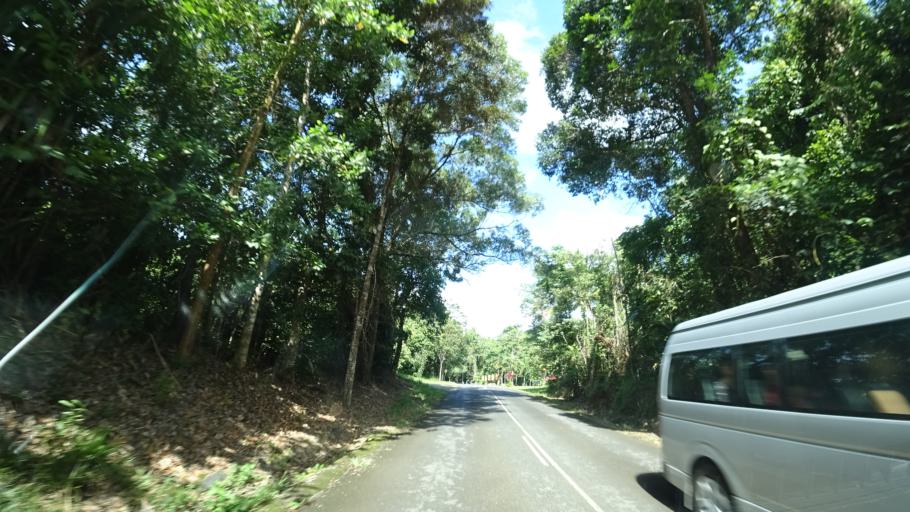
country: AU
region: Queensland
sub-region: Cairns
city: Port Douglas
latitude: -16.2006
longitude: 145.4118
